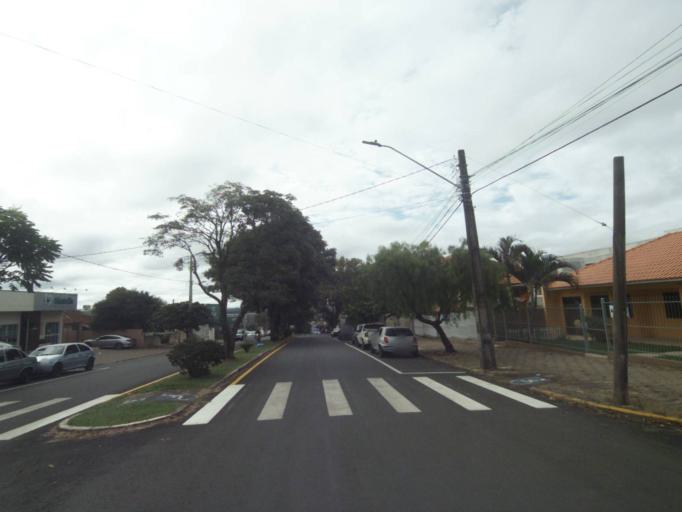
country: BR
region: Parana
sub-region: Telemaco Borba
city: Telemaco Borba
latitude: -24.3302
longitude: -50.6192
